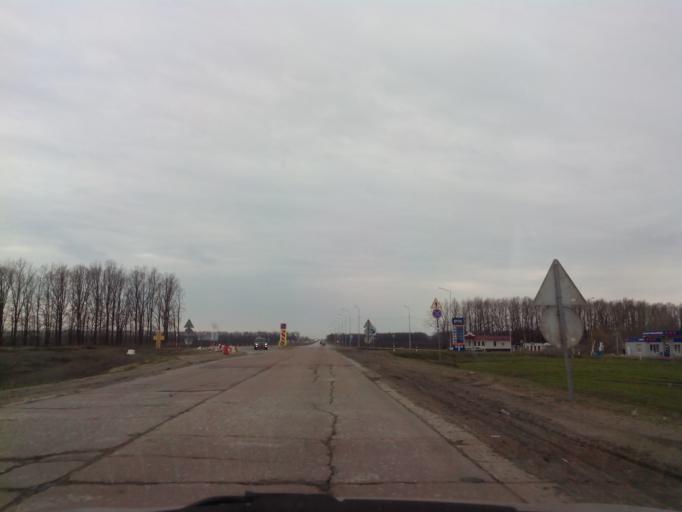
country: RU
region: Tambov
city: Zavoronezhskoye
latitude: 52.8912
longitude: 40.6971
